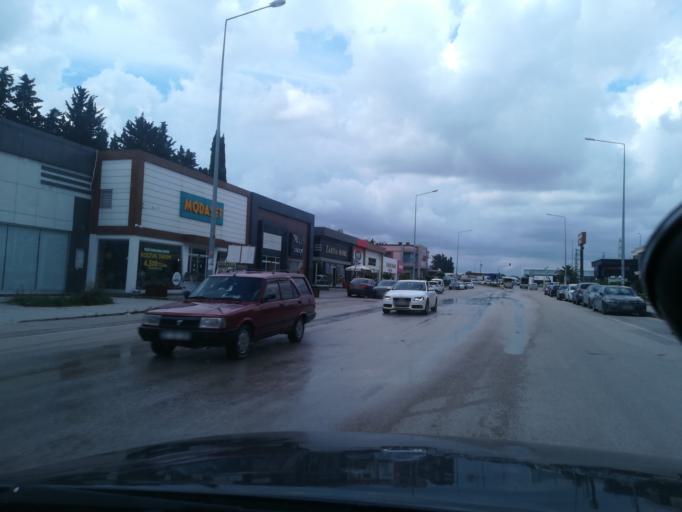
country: TR
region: Adana
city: Yuregir
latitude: 36.9814
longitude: 35.3941
